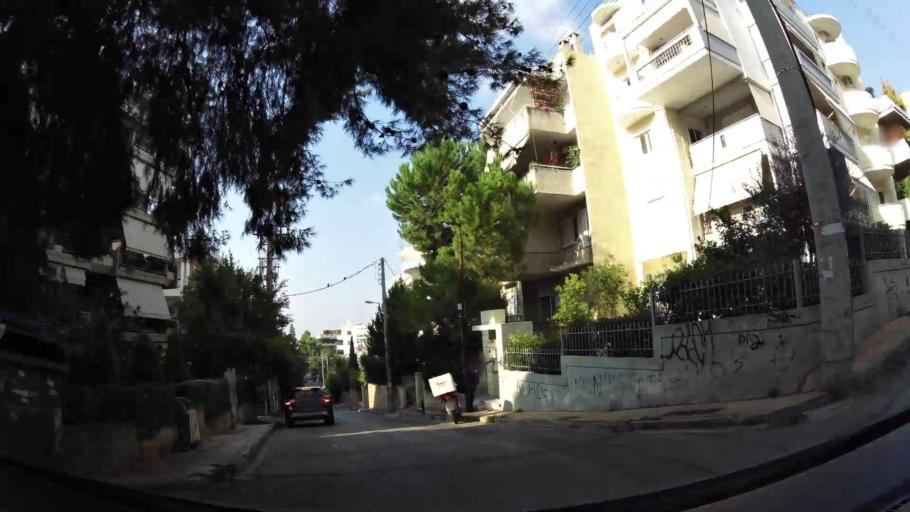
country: GR
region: Attica
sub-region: Nomarchia Athinas
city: Cholargos
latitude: 38.0056
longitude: 23.8165
